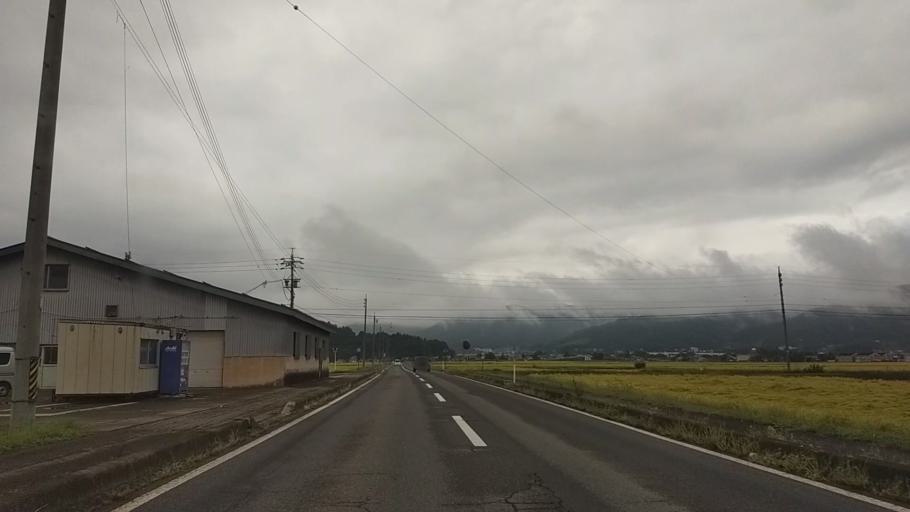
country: JP
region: Nagano
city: Iiyama
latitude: 36.8481
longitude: 138.3832
